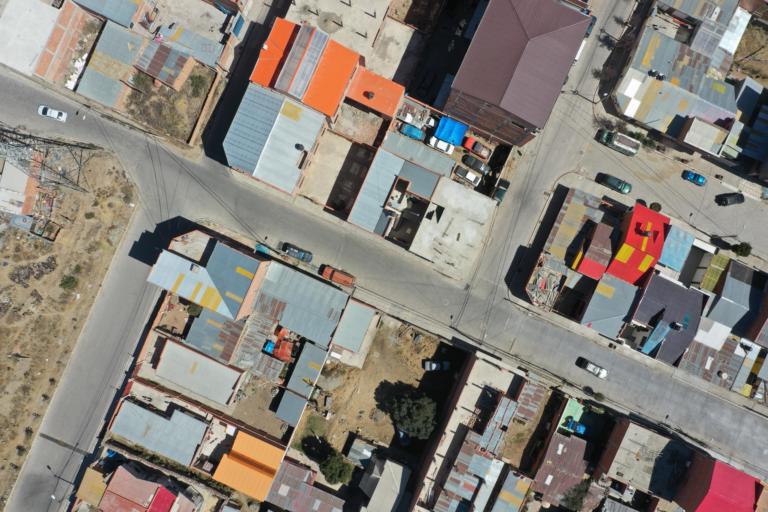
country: BO
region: La Paz
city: La Paz
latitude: -16.5346
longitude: -68.1517
